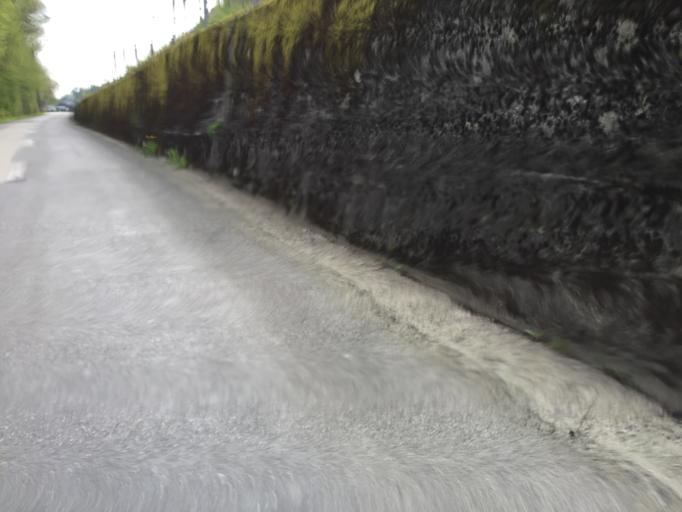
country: CH
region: Fribourg
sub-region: Sense District
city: Flamatt
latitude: 46.8890
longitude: 7.3150
